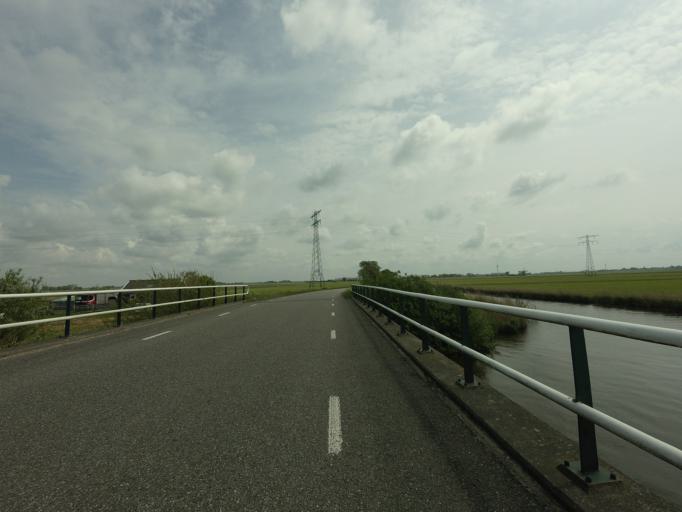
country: NL
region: Friesland
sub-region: Sudwest Fryslan
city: Bolsward
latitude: 53.1070
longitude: 5.5043
